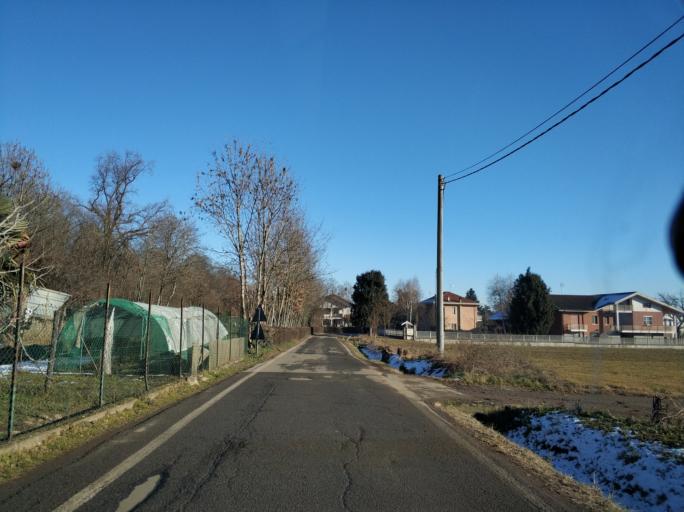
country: IT
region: Piedmont
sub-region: Provincia di Torino
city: San Francesco al Campo
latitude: 45.2192
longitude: 7.6709
